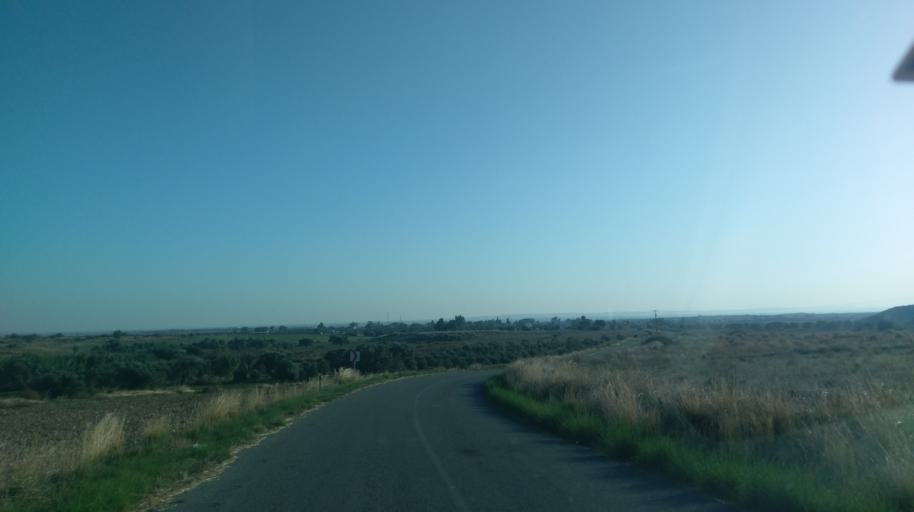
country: CY
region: Ammochostos
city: Lefkonoiko
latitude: 35.2792
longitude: 33.6588
